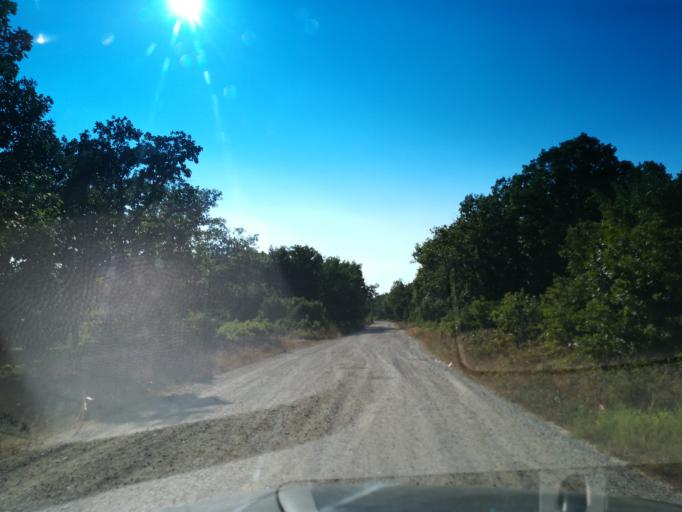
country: BG
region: Khaskovo
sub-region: Obshtina Mineralni Bani
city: Mineralni Bani
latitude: 41.9716
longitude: 25.3331
